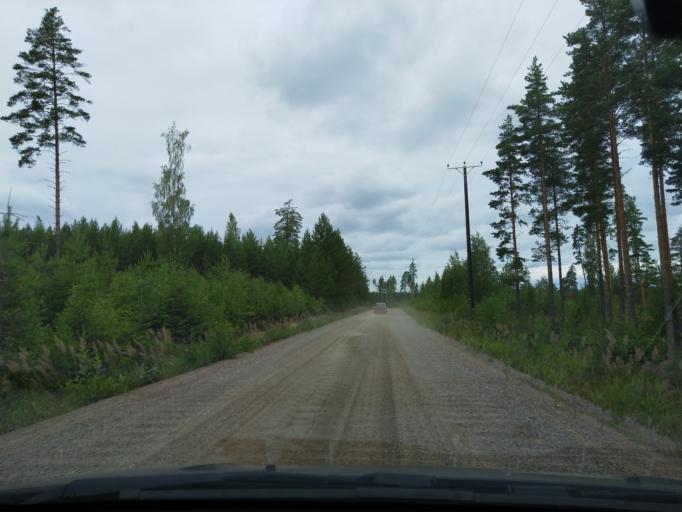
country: FI
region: Southern Savonia
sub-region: Mikkeli
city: Maentyharju
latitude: 61.1310
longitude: 26.8938
